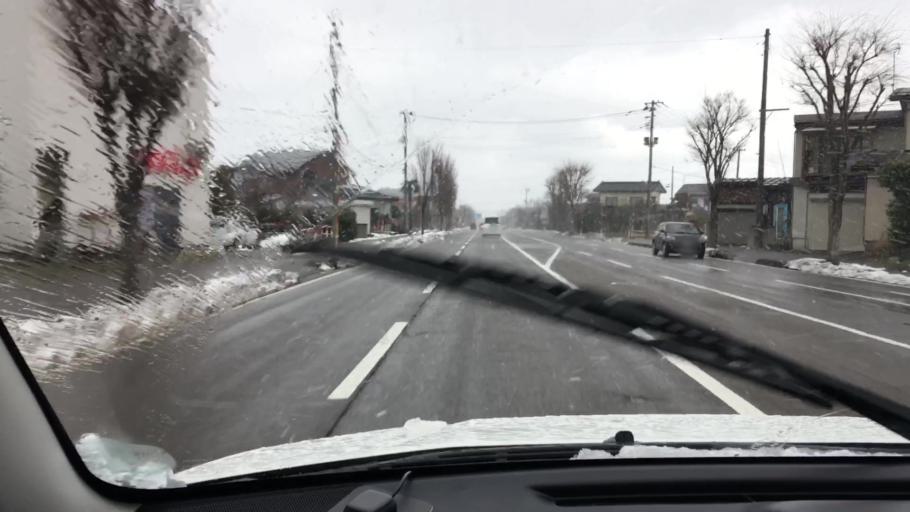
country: JP
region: Niigata
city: Joetsu
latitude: 37.1178
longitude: 138.2328
